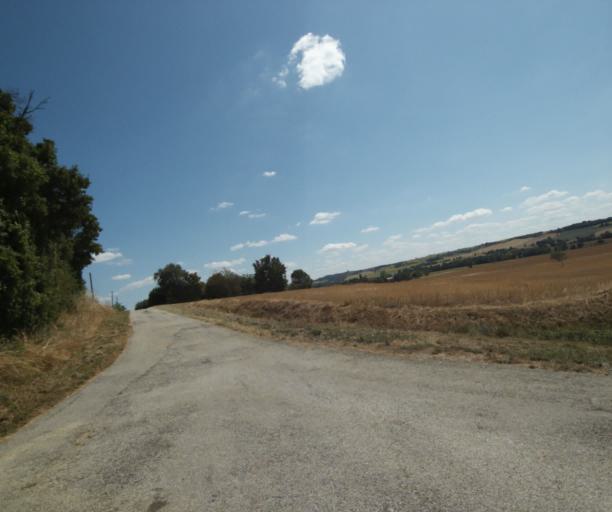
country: FR
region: Midi-Pyrenees
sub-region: Departement de la Haute-Garonne
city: Saint-Felix-Lauragais
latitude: 43.4897
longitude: 1.8872
